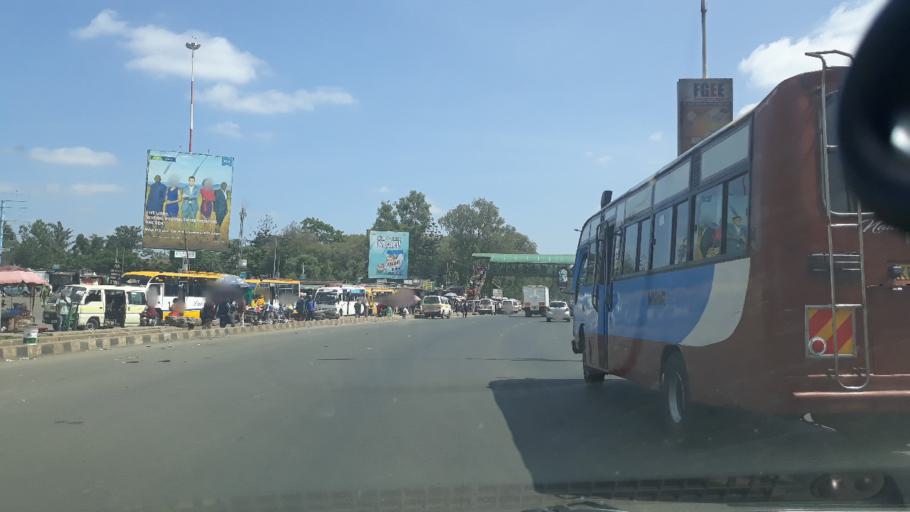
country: KE
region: Nairobi Area
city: Nairobi
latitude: -1.2754
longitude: 36.8232
